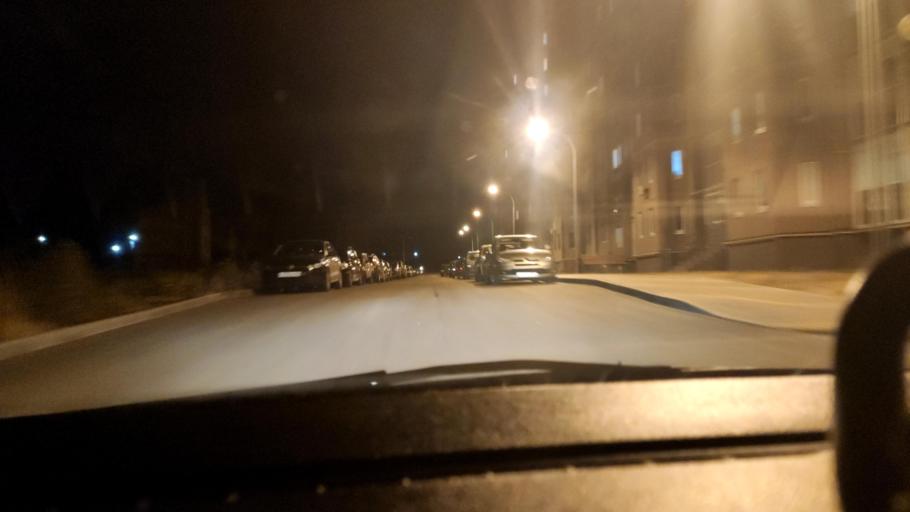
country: RU
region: Voronezj
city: Shilovo
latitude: 51.5744
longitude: 39.1290
